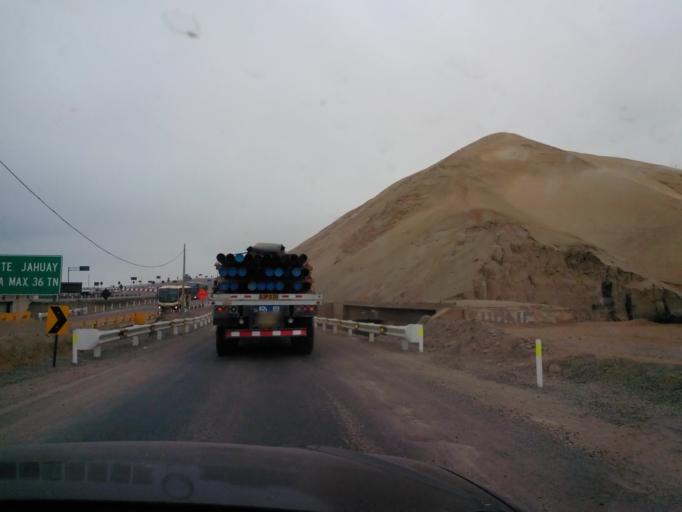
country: PE
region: Ica
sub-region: Provincia de Chincha
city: San Pedro
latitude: -13.3232
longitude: -76.2430
